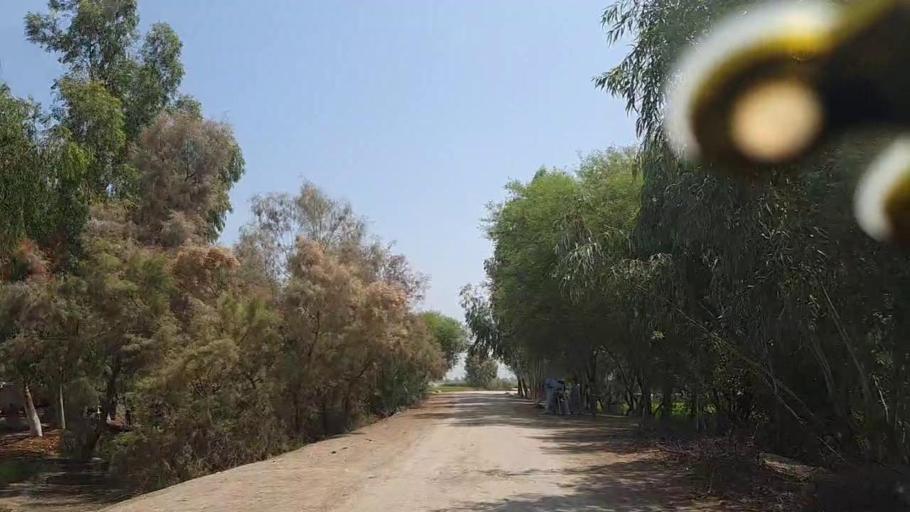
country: PK
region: Sindh
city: Rustam jo Goth
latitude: 28.1087
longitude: 68.8836
